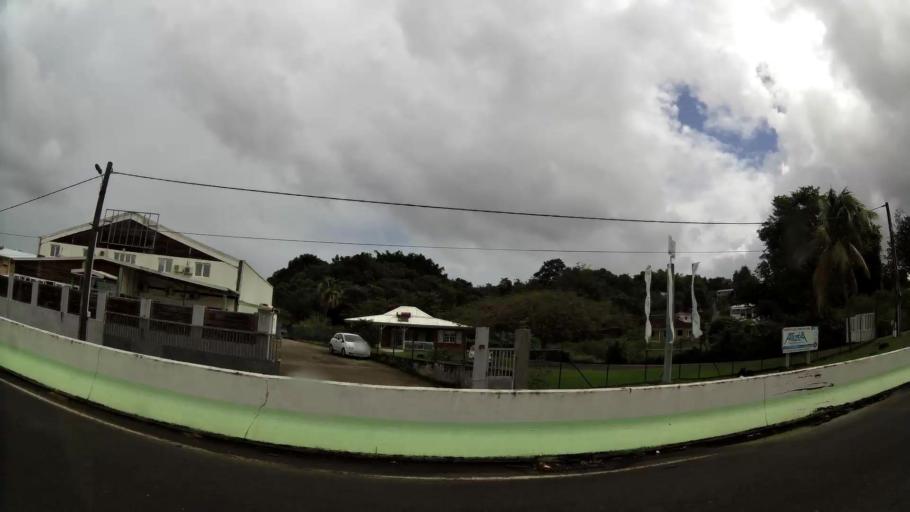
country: MQ
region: Martinique
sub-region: Martinique
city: Ducos
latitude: 14.5878
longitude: -60.9816
